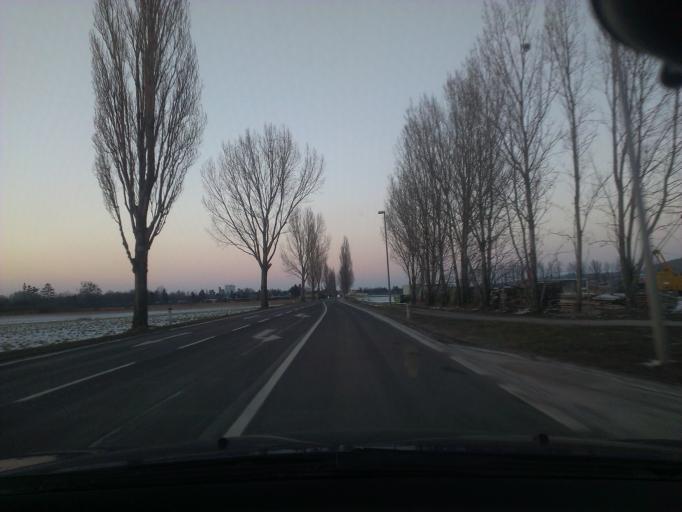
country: AT
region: Lower Austria
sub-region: Politischer Bezirk Bruck an der Leitha
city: Enzersdorf an der Fischa
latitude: 48.0701
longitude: 16.6093
